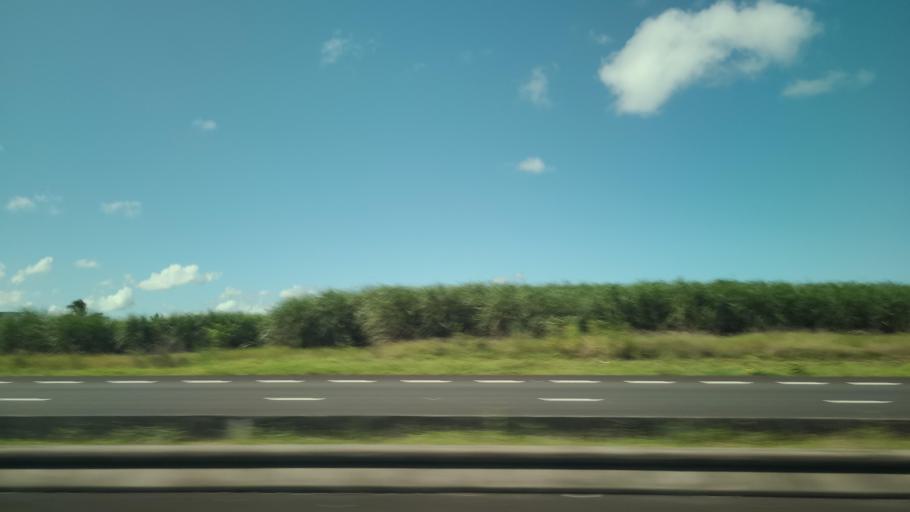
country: MU
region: Grand Port
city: Plaine Magnien
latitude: -20.4394
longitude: 57.6638
